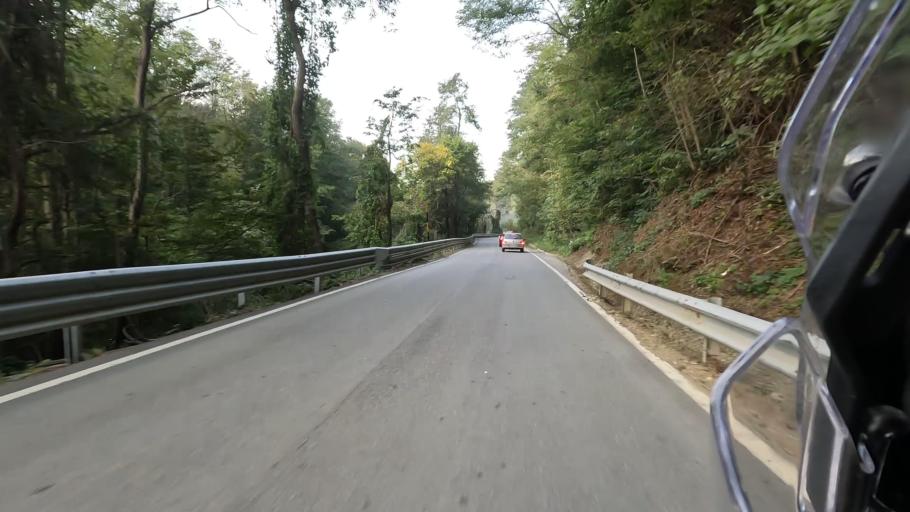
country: IT
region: Liguria
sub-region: Provincia di Savona
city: Sassello
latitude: 44.4618
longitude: 8.4822
